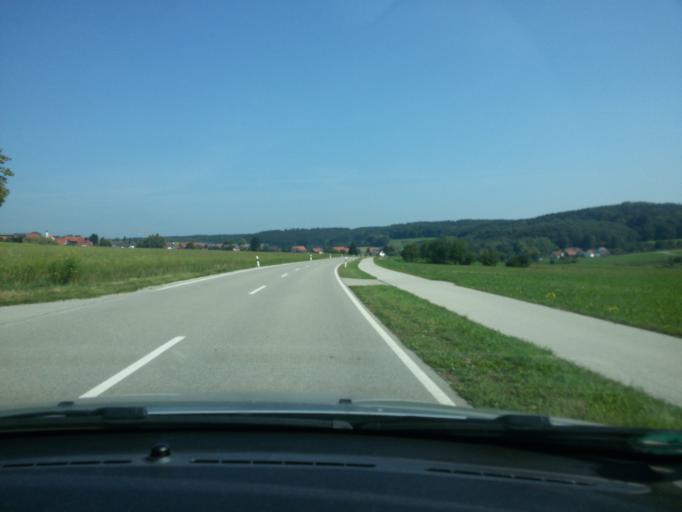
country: DE
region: Bavaria
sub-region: Swabia
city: Scherstetten
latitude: 48.1995
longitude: 10.6446
